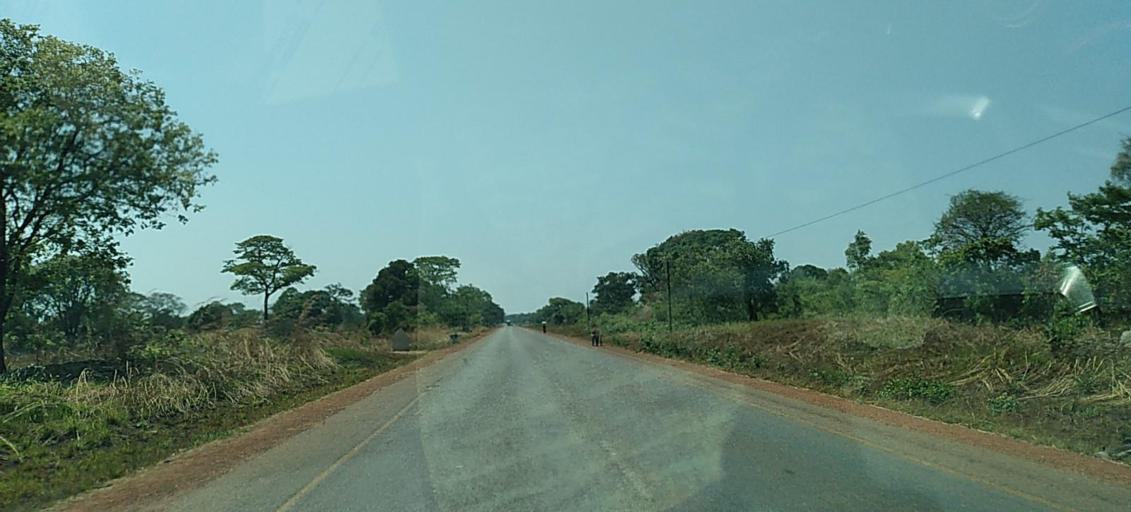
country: ZM
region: North-Western
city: Solwezi
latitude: -12.3543
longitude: 25.9254
